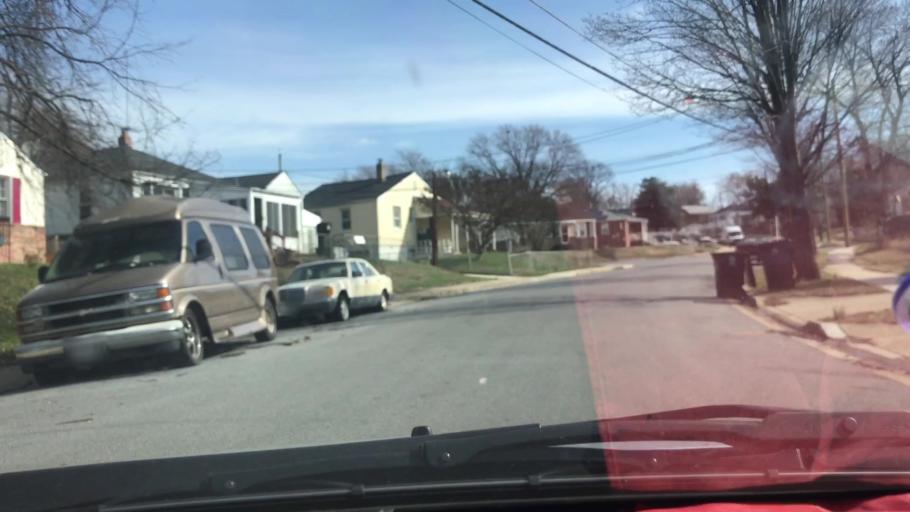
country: US
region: Maryland
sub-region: Prince George's County
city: Fairmount Heights
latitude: 38.9070
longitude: -76.9224
